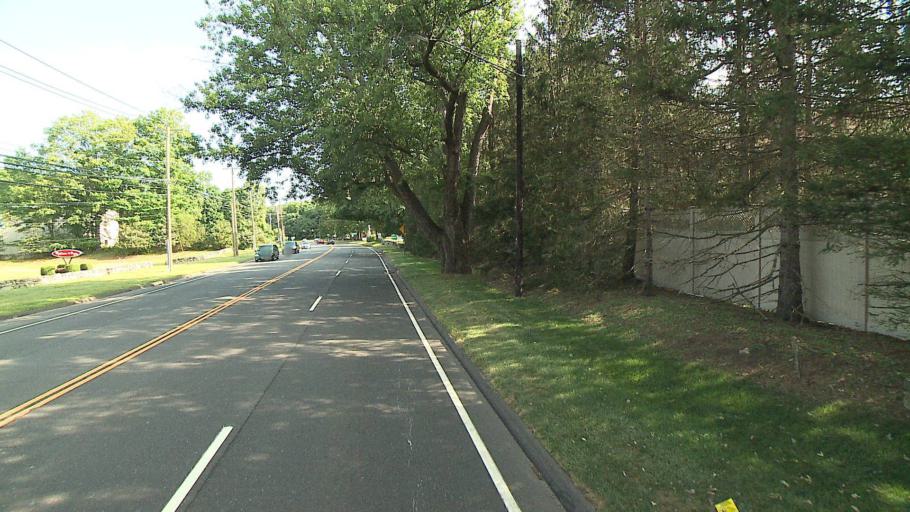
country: US
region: Connecticut
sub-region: Fairfield County
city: Wilton
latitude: 41.1793
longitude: -73.4161
